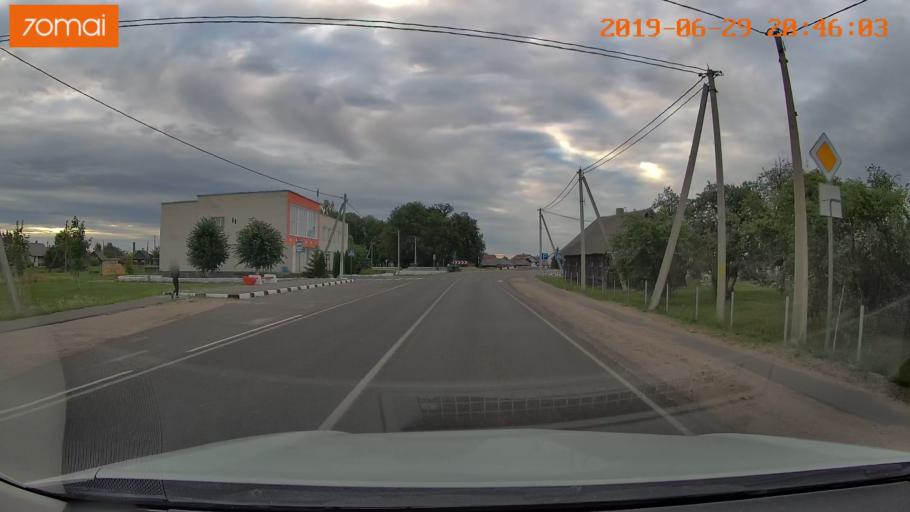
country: BY
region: Brest
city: Hantsavichy
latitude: 52.6285
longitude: 26.3076
